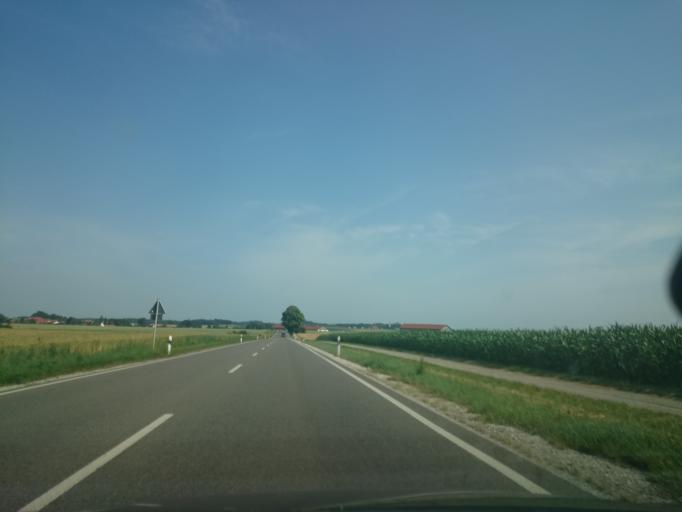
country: DE
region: Bavaria
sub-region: Swabia
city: Merching
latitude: 48.2407
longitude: 10.9990
